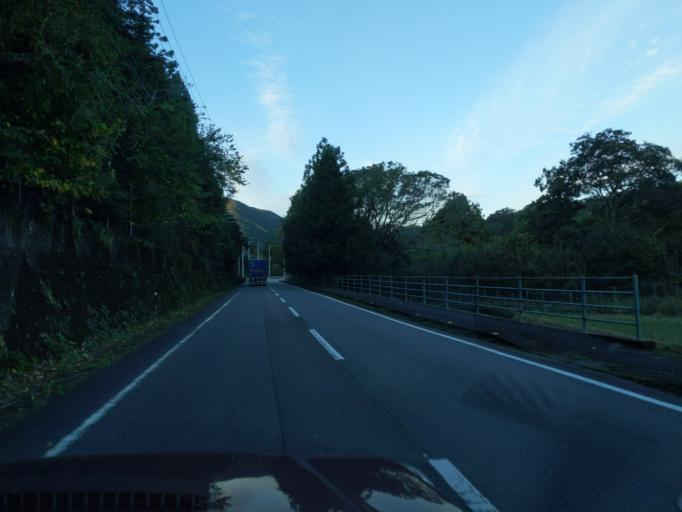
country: JP
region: Tokushima
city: Anan
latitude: 33.6904
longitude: 134.4312
